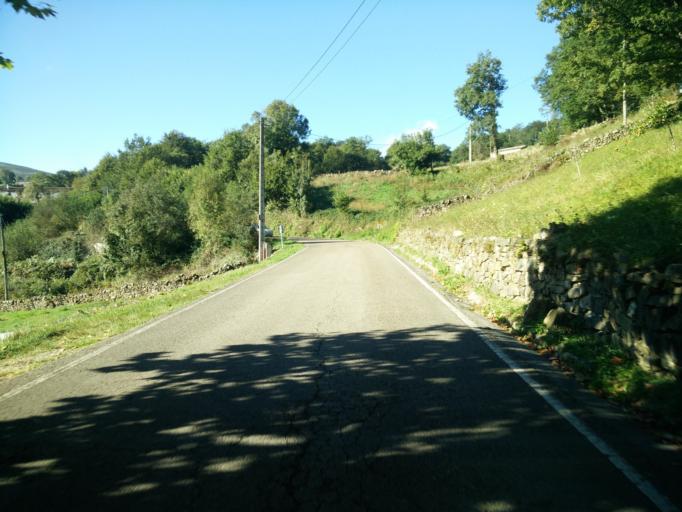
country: ES
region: Cantabria
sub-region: Provincia de Cantabria
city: San Pedro del Romeral
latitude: 43.1165
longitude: -3.8073
